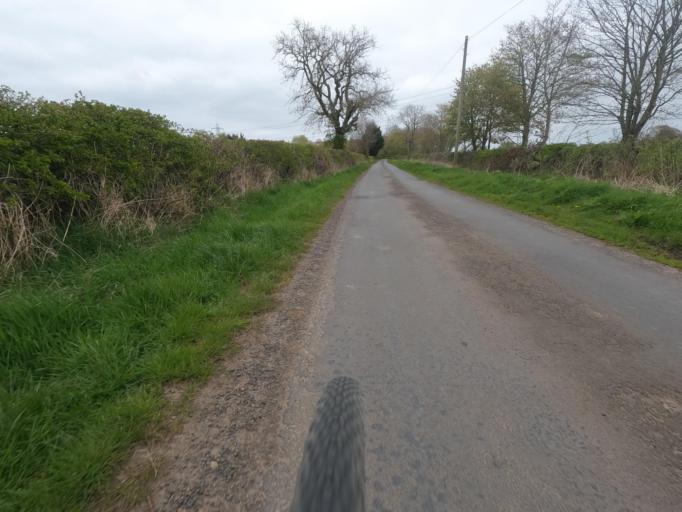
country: GB
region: England
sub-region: Northumberland
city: Horsley
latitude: 55.0631
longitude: -1.8417
